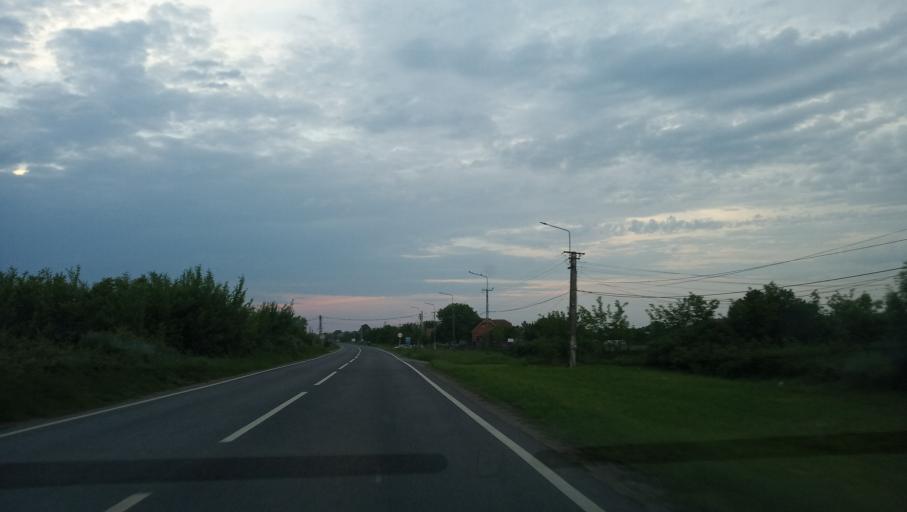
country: RO
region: Timis
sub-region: Comuna Jebel
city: Jebel
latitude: 45.5513
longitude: 21.2225
